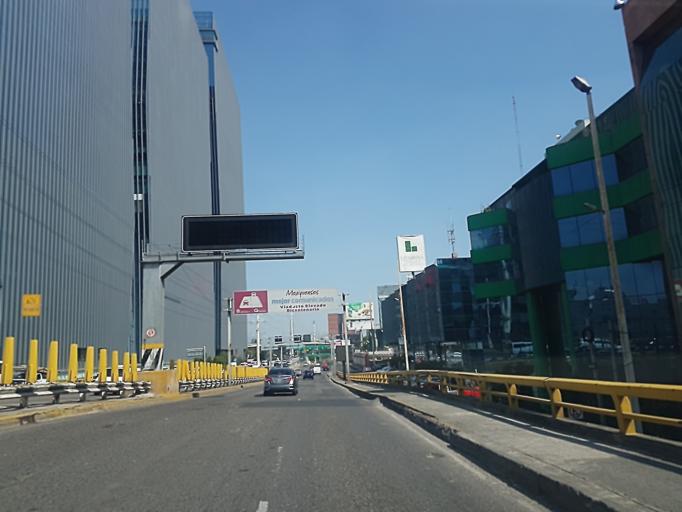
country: MX
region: Mexico City
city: Miguel Hidalgo
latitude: 19.4544
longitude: -99.2172
